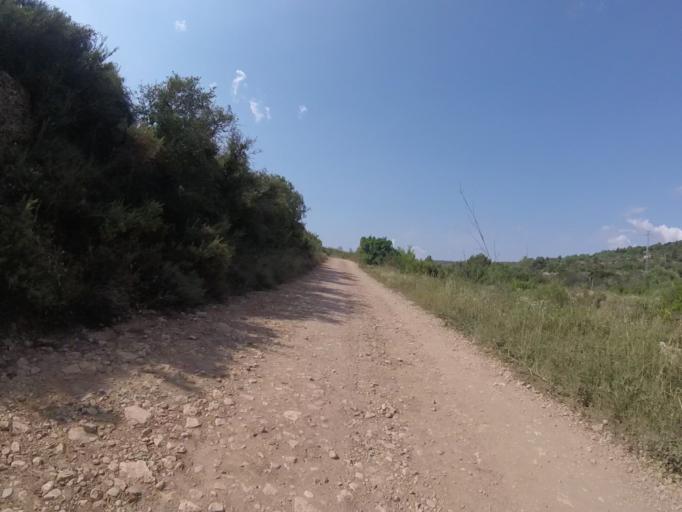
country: ES
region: Valencia
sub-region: Provincia de Castello
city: Cuevas de Vinroma
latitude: 40.3020
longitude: 0.1667
